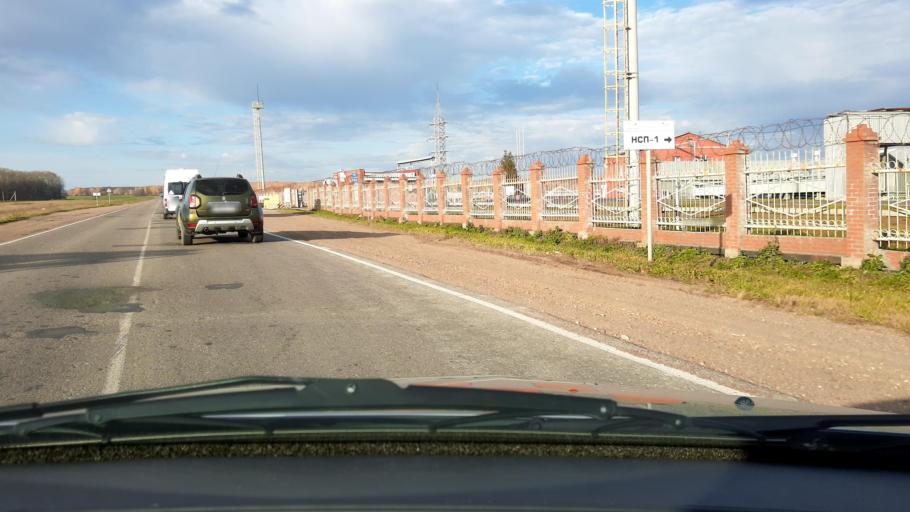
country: RU
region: Bashkortostan
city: Mikhaylovka
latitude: 54.8241
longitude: 55.7645
